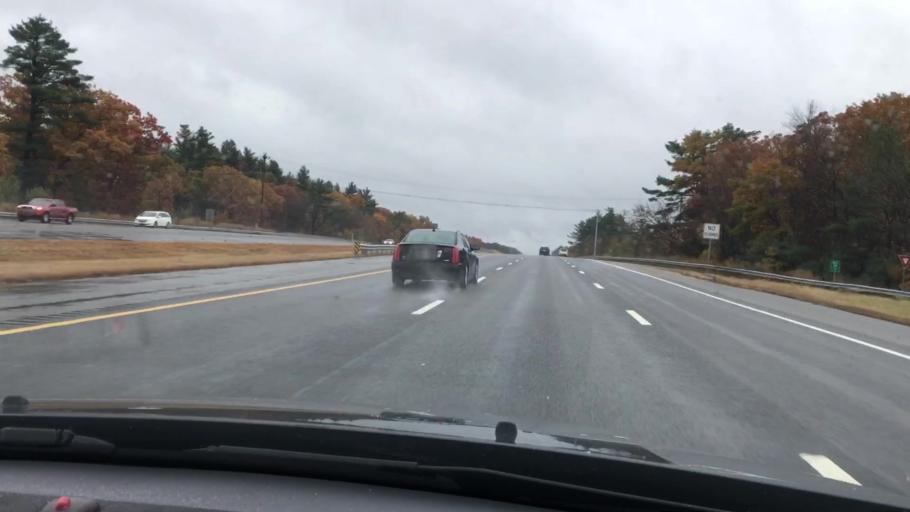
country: US
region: Massachusetts
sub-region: Middlesex County
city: Tyngsboro
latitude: 42.6601
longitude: -71.4297
